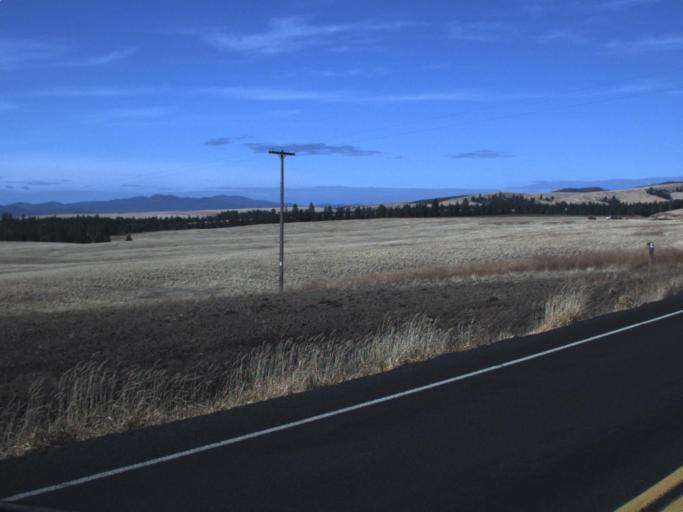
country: US
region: Washington
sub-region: Lincoln County
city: Davenport
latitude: 47.8024
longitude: -118.1738
